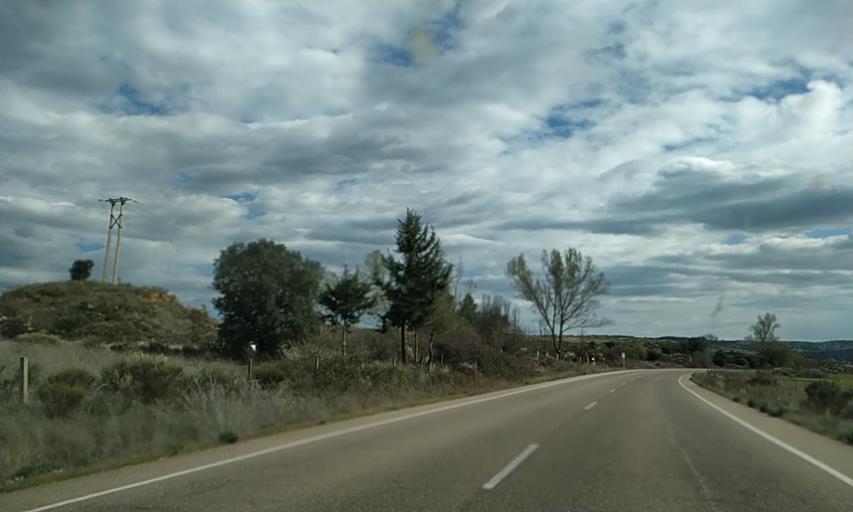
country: ES
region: Castille and Leon
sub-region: Provincia de Salamanca
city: Pastores
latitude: 40.5291
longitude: -6.5667
